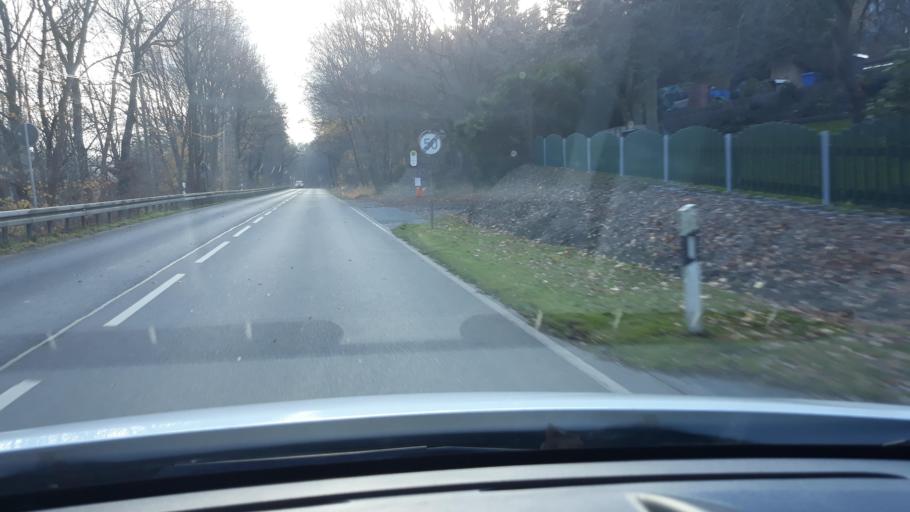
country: DE
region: Saxony
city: Wilkau-Hasslau
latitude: 50.6603
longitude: 12.5241
